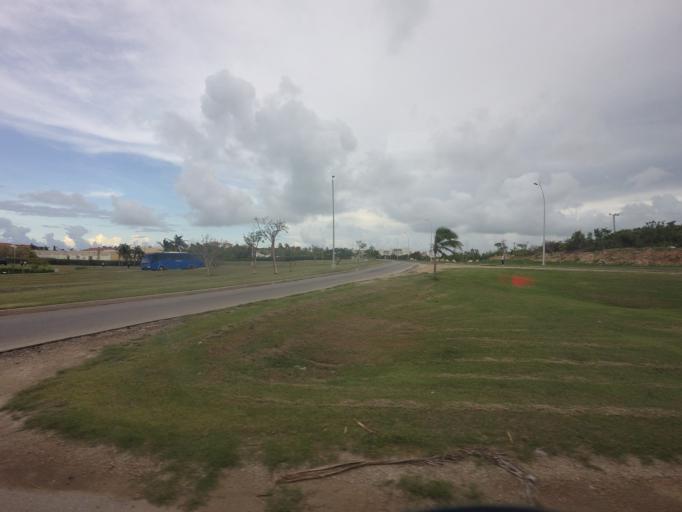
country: CU
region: Matanzas
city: Varadero
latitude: 23.1977
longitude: -81.1345
